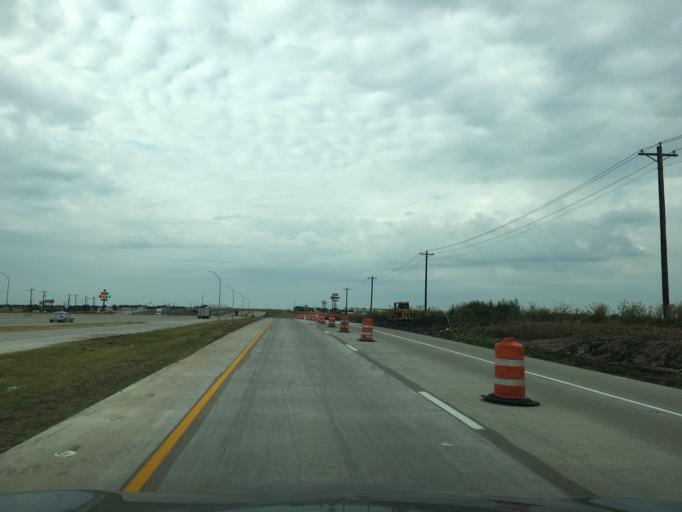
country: US
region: Texas
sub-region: Collin County
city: Anna
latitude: 33.3512
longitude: -96.5860
